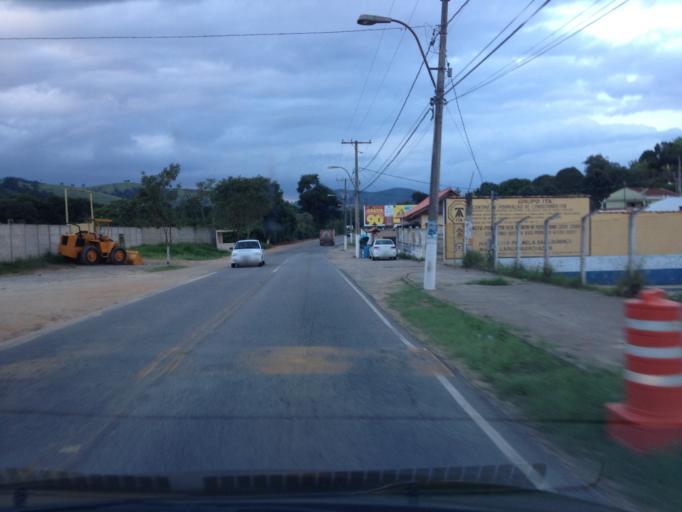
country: BR
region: Minas Gerais
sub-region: Sao Lourenco
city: Sao Lourenco
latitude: -22.0995
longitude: -45.0507
